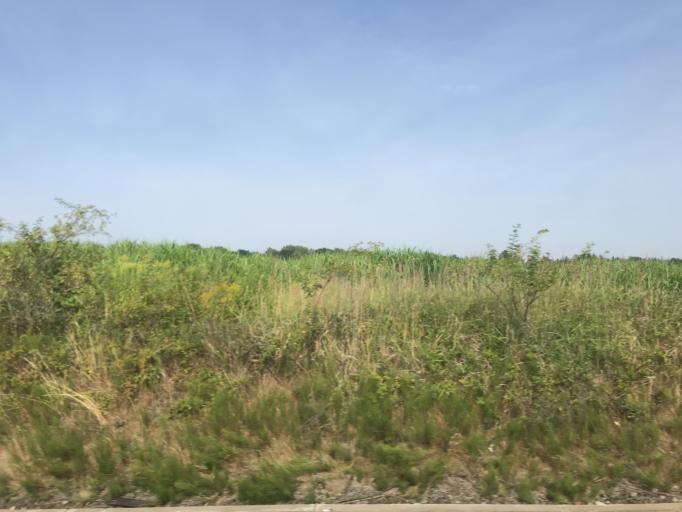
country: CZ
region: Central Bohemia
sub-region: Okres Praha-Vychod
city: Ricany
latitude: 49.9767
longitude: 14.6658
